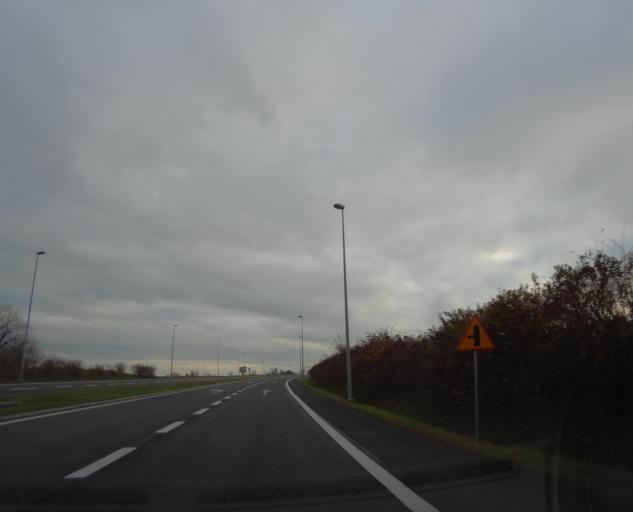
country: PL
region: Subcarpathian Voivodeship
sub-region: Powiat jaroslawski
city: Radymno
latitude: 49.9335
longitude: 22.8191
